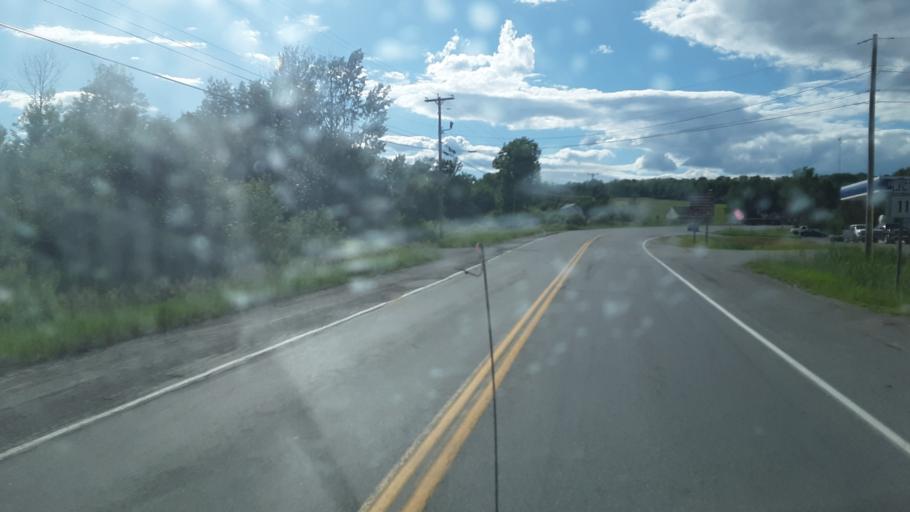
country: US
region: Maine
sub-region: Penobscot County
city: Patten
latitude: 45.8738
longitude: -68.4153
